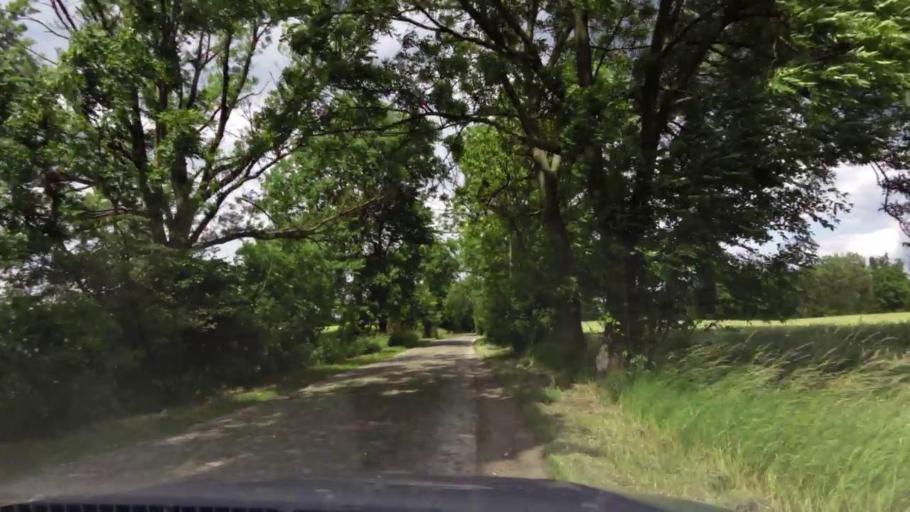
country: PL
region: West Pomeranian Voivodeship
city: Trzcinsko Zdroj
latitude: 52.9568
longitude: 14.7134
